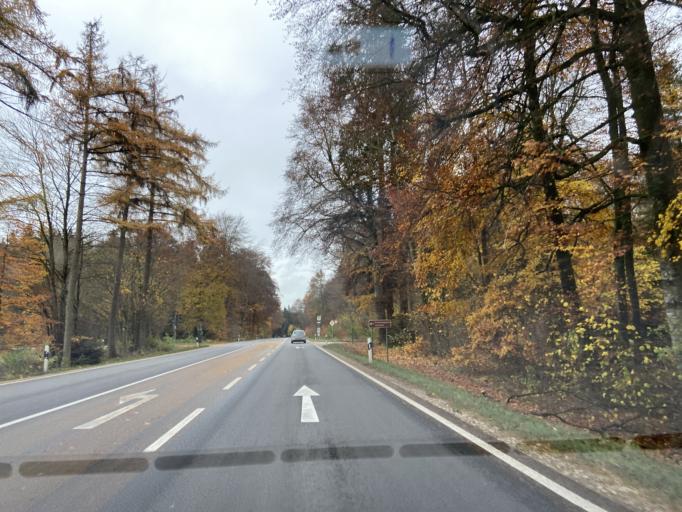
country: DE
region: Baden-Wuerttemberg
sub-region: Tuebingen Region
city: Krauchenwies
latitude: 48.0561
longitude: 9.2313
